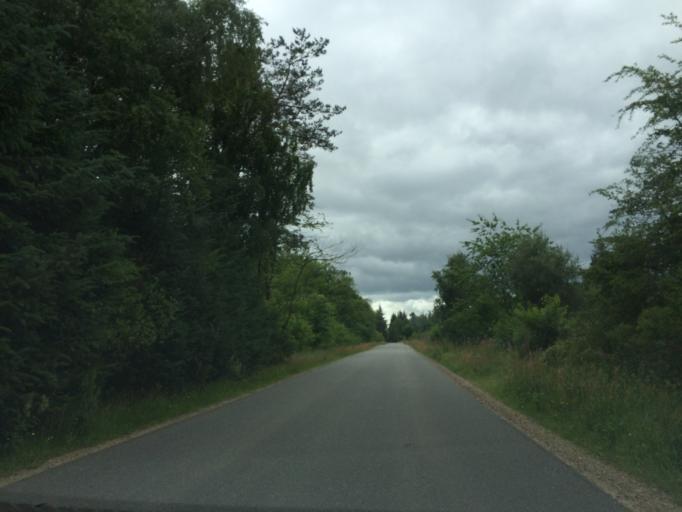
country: DK
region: Central Jutland
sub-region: Silkeborg Kommune
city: Svejbaek
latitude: 56.2307
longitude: 9.6814
